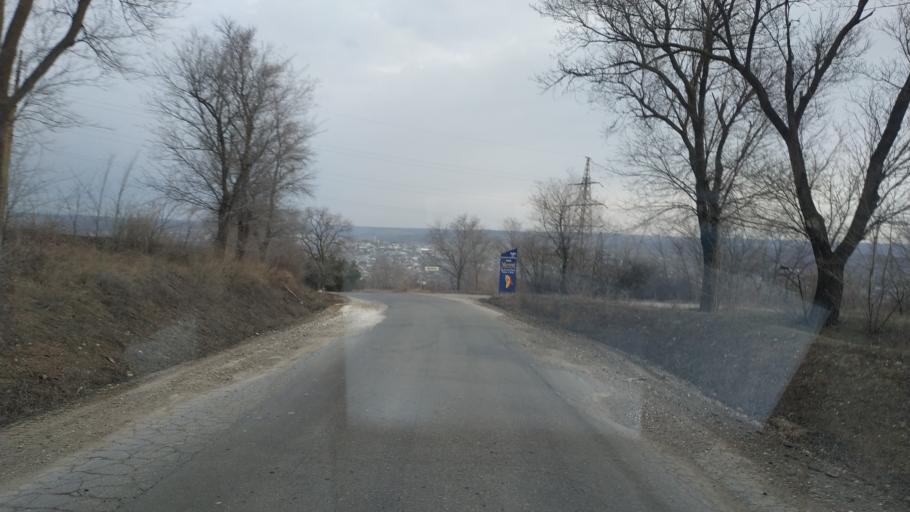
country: MD
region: Chisinau
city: Singera
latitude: 46.9505
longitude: 29.0573
